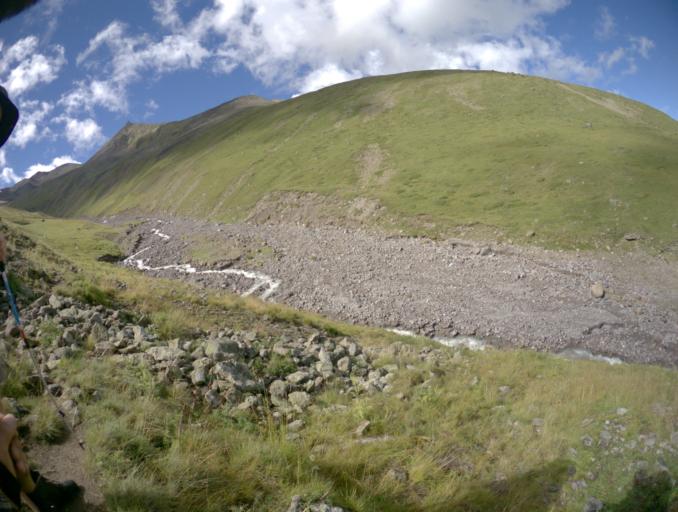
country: RU
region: Kabardino-Balkariya
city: Terskol
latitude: 43.3960
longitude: 42.3618
